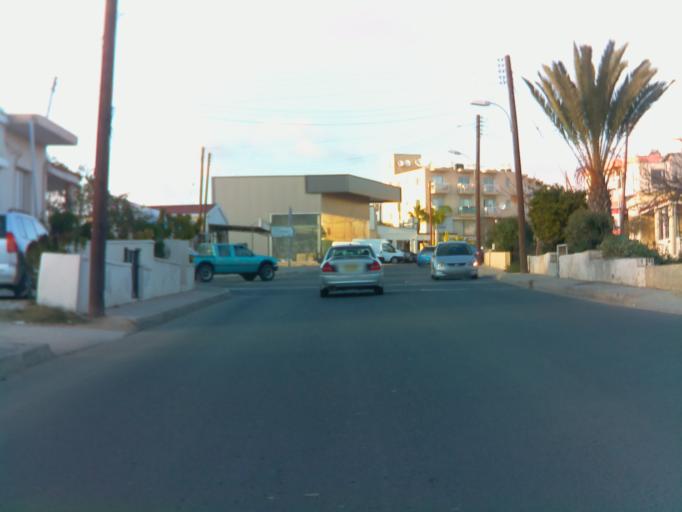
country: CY
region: Pafos
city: Paphos
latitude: 34.7830
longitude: 32.4217
